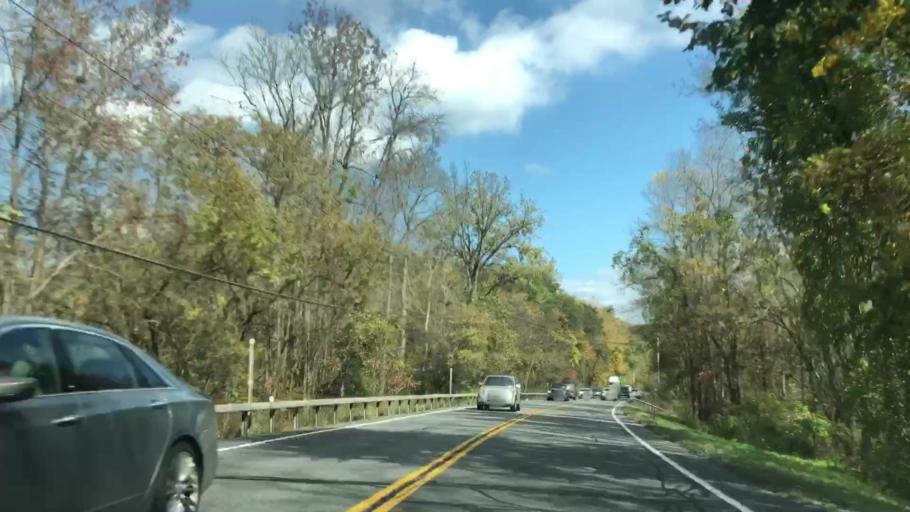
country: US
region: New York
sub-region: Warren County
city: Queensbury
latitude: 43.4235
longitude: -73.4832
